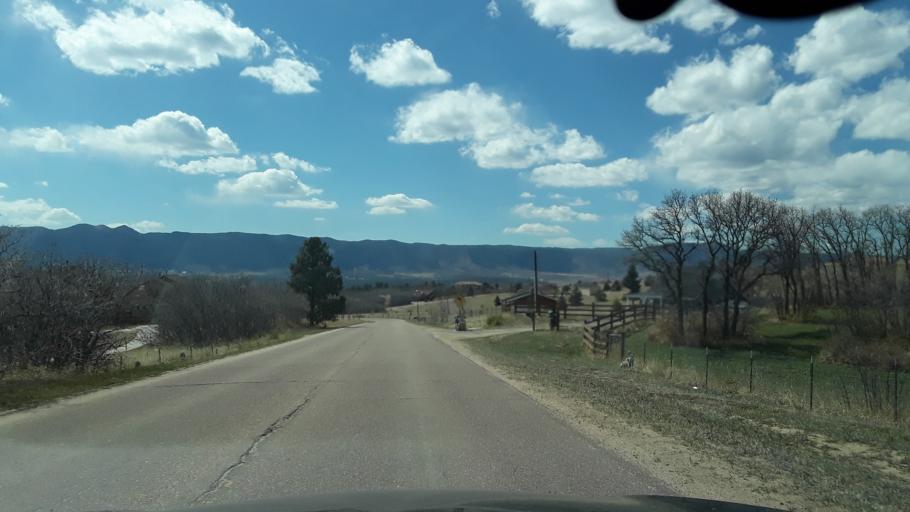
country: US
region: Colorado
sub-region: El Paso County
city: Gleneagle
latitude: 39.0347
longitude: -104.7871
